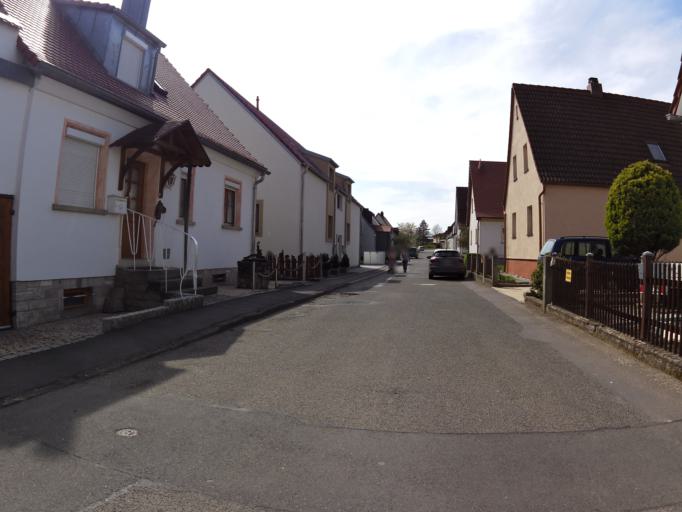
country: DE
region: Bavaria
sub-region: Regierungsbezirk Unterfranken
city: Unterpleichfeld
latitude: 49.8699
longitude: 10.0412
